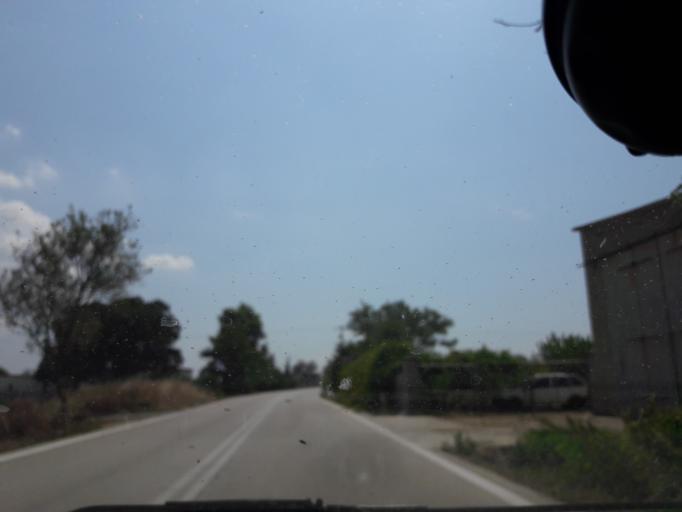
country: GR
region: North Aegean
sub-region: Nomos Lesvou
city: Myrina
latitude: 39.9311
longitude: 25.3394
